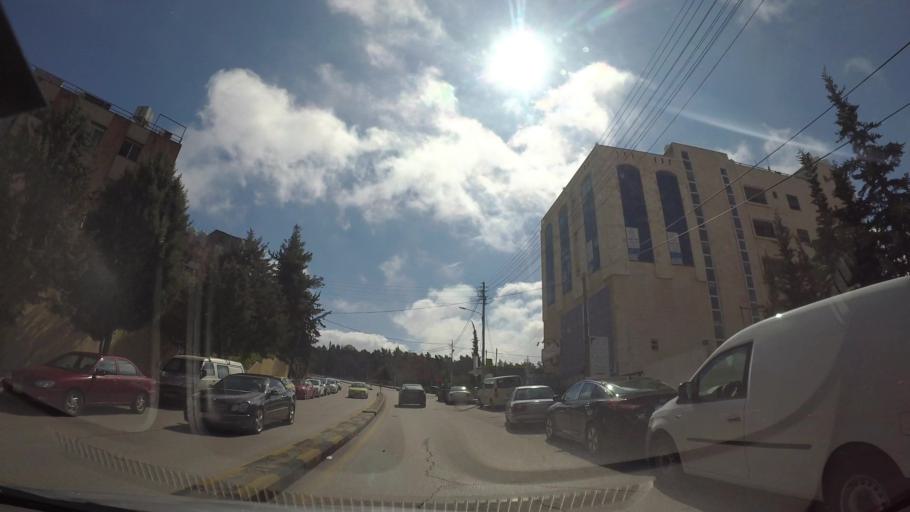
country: JO
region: Amman
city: Al Jubayhah
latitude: 32.0561
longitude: 35.8735
